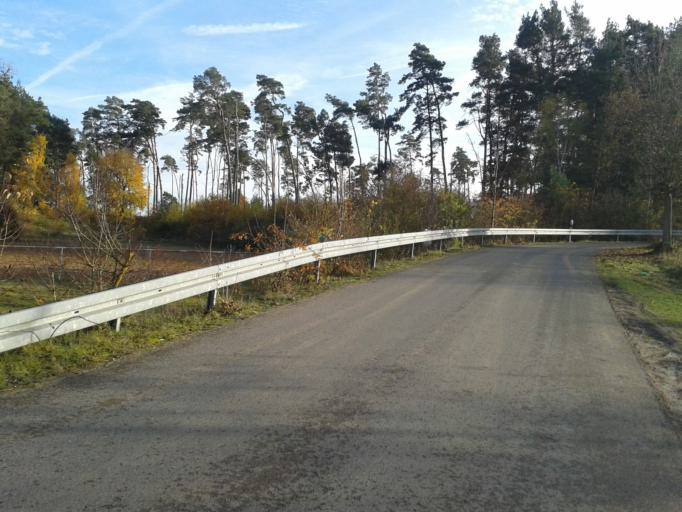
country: DE
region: Bavaria
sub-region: Upper Franconia
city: Gundelsheim
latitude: 49.9268
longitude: 10.8989
